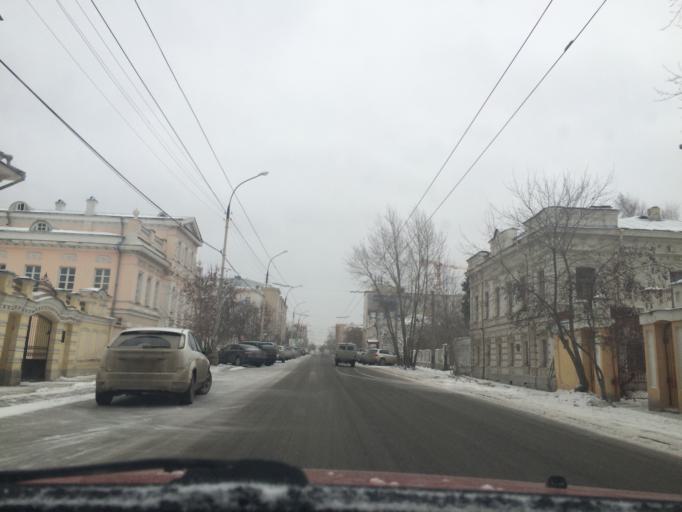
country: RU
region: Sverdlovsk
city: Yekaterinburg
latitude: 56.8225
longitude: 60.6115
